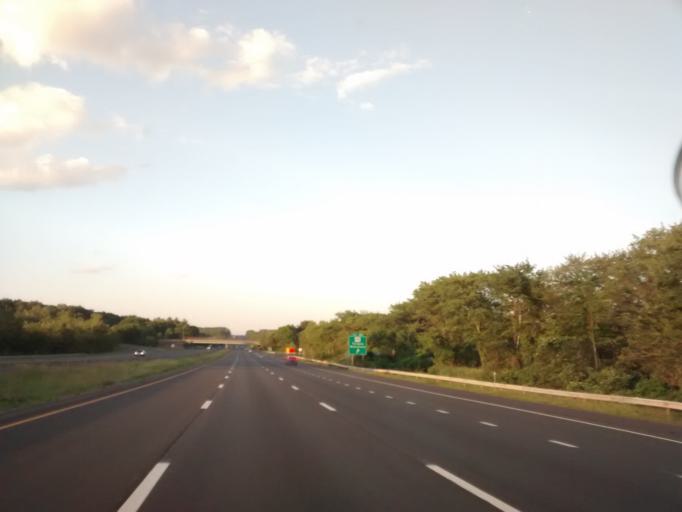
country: US
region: Connecticut
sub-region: Tolland County
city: Tolland
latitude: 41.8613
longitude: -72.3665
